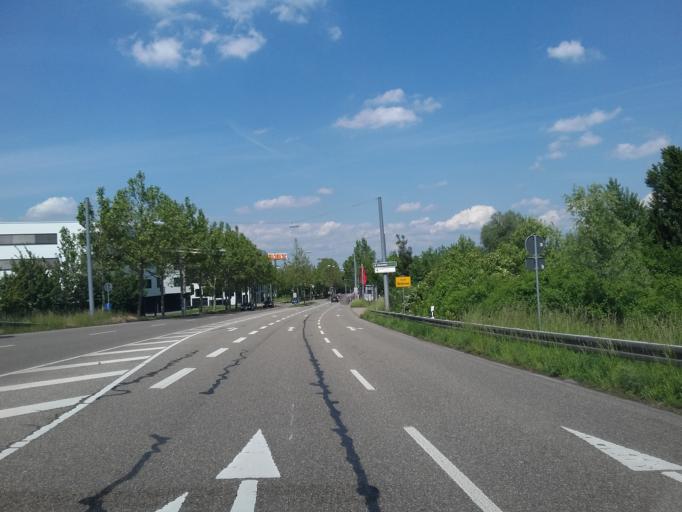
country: DE
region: Baden-Wuerttemberg
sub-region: Regierungsbezirk Stuttgart
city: Flein
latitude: 49.1192
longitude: 9.2224
